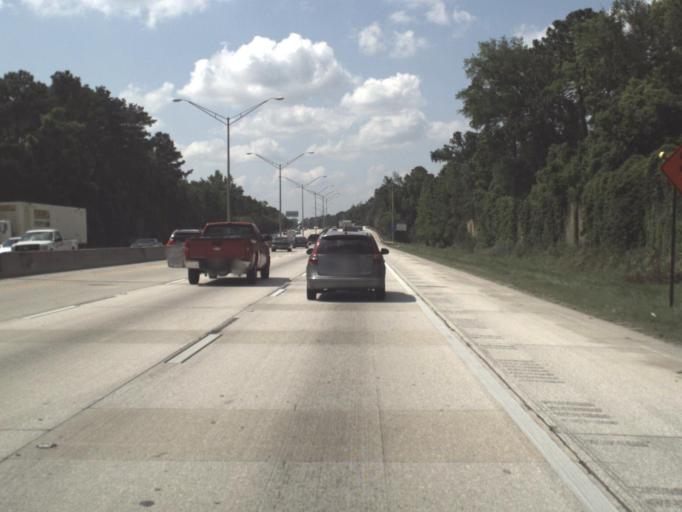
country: US
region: Florida
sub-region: Duval County
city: Jacksonville
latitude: 30.2787
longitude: -81.6186
